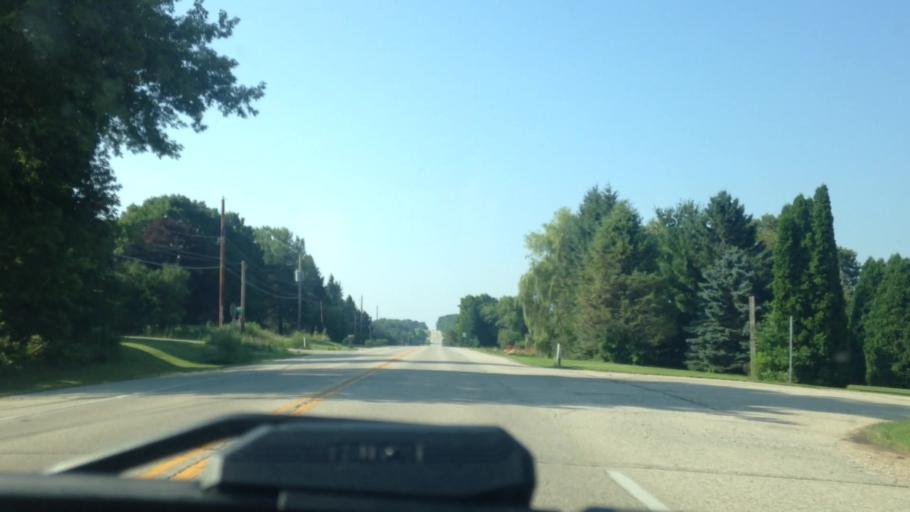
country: US
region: Wisconsin
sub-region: Washington County
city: Richfield
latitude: 43.2467
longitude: -88.2618
